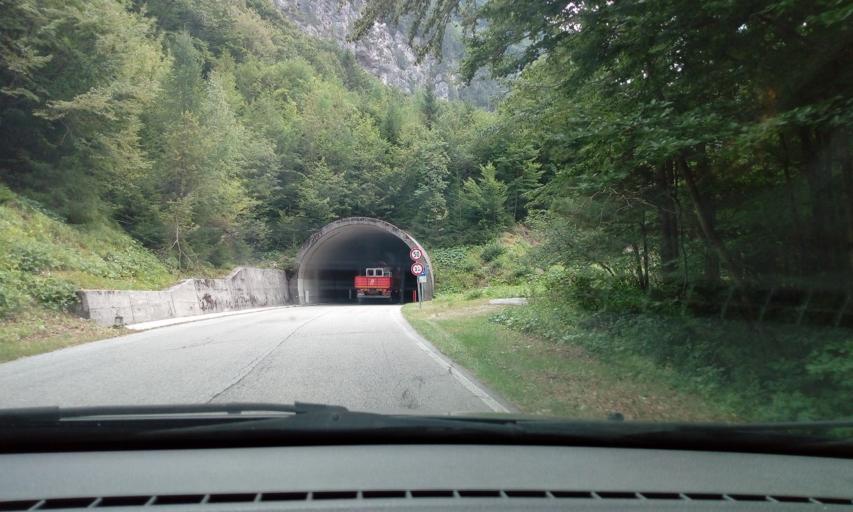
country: SI
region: Bovec
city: Bovec
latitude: 46.3937
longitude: 13.4574
